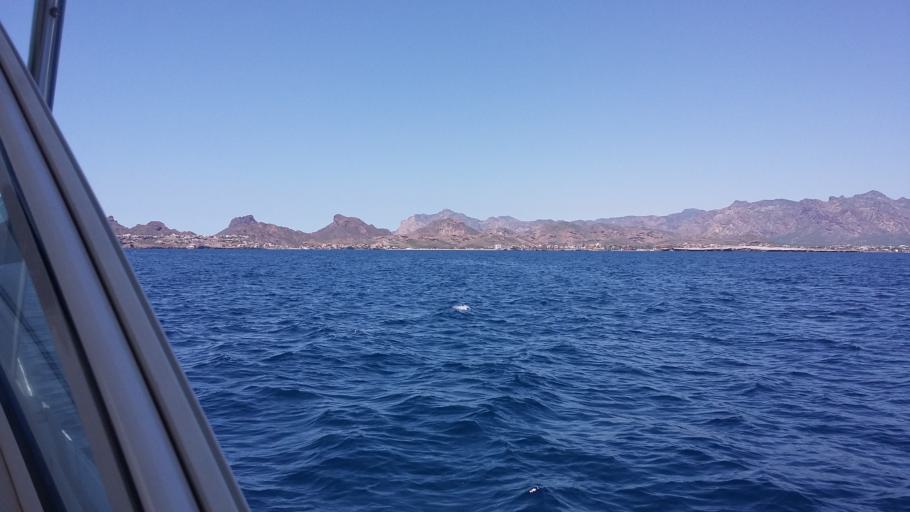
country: MX
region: Sonora
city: Heroica Guaymas
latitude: 27.9282
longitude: -111.0162
